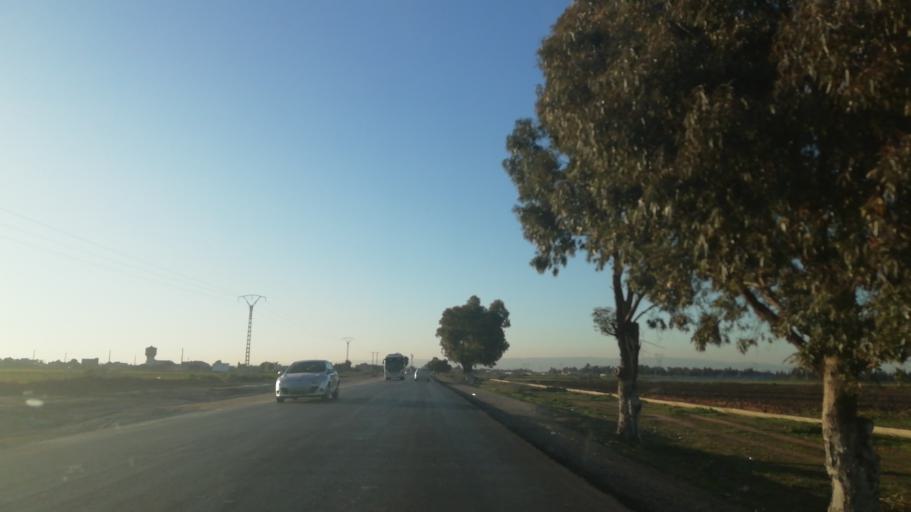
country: DZ
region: Relizane
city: Relizane
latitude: 35.7630
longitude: 0.6486
